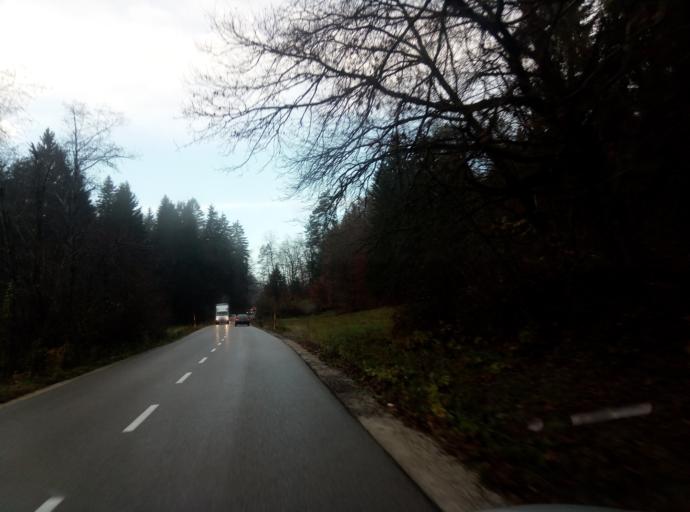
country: SI
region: Menges
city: Menges
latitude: 46.1705
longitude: 14.5514
